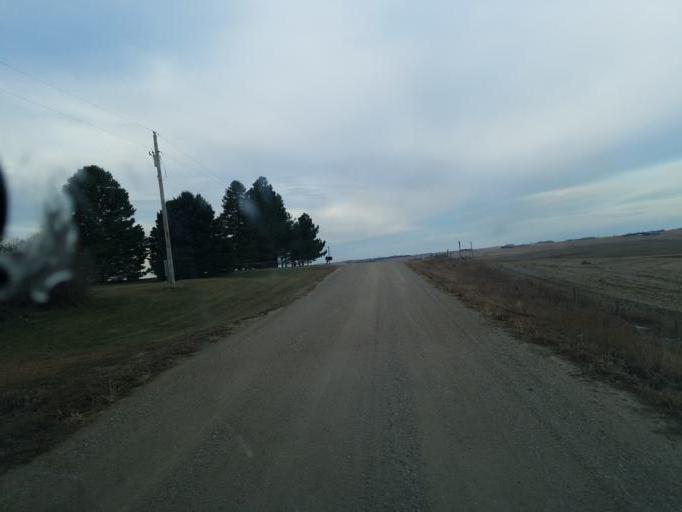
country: US
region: Nebraska
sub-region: Knox County
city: Bloomfield
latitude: 42.5833
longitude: -97.6409
